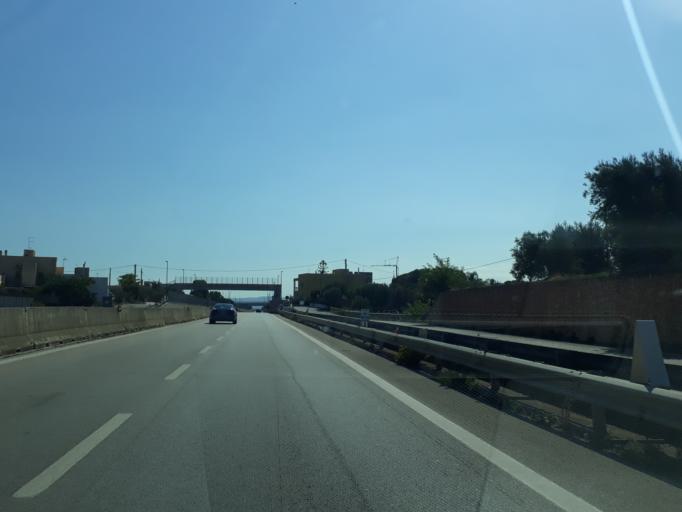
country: IT
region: Apulia
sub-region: Provincia di Brindisi
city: Fasano
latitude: 40.8859
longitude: 17.3353
